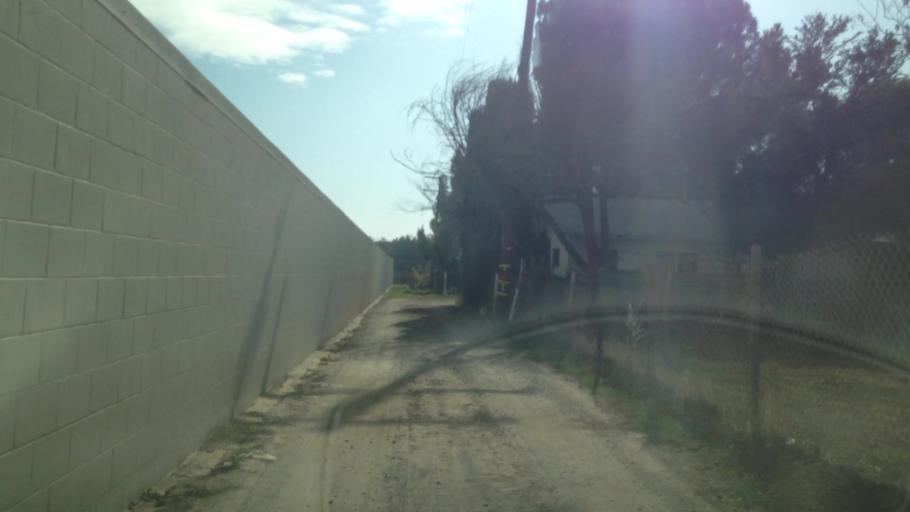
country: US
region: California
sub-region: Riverside County
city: Beaumont
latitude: 33.9288
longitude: -116.9635
